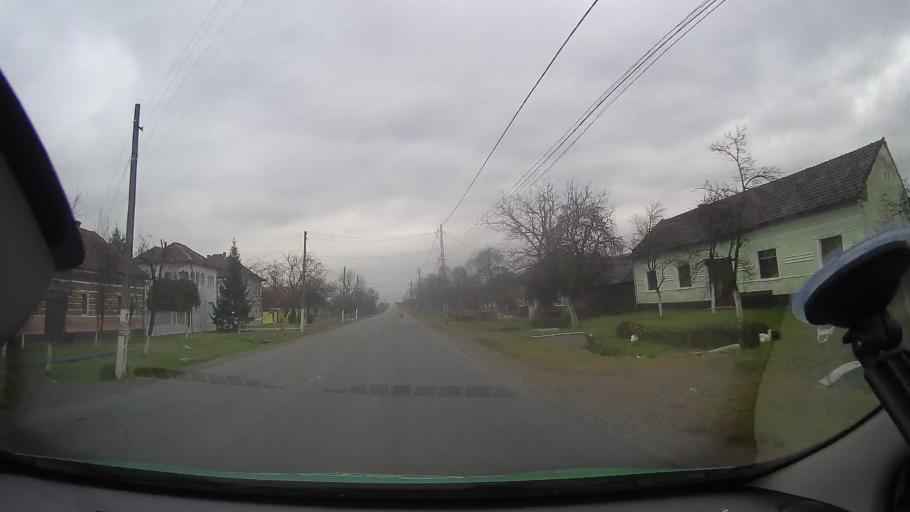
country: RO
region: Arad
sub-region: Comuna Almas
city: Almas
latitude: 46.2826
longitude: 22.2685
